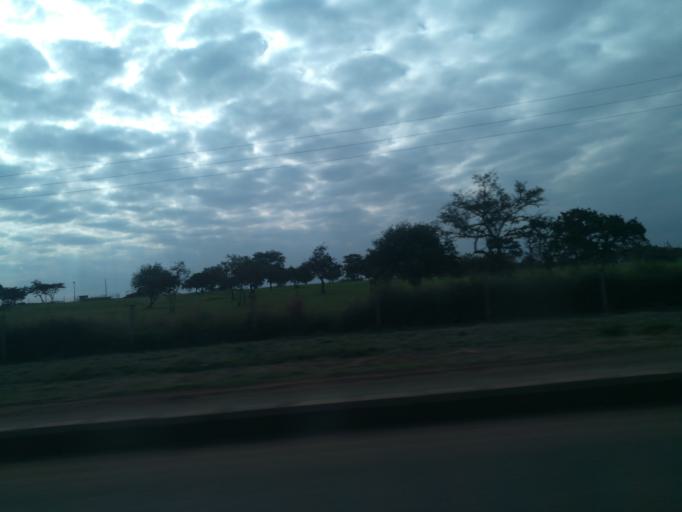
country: KE
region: Nairobi Area
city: Thika
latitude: -1.1267
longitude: 37.0007
